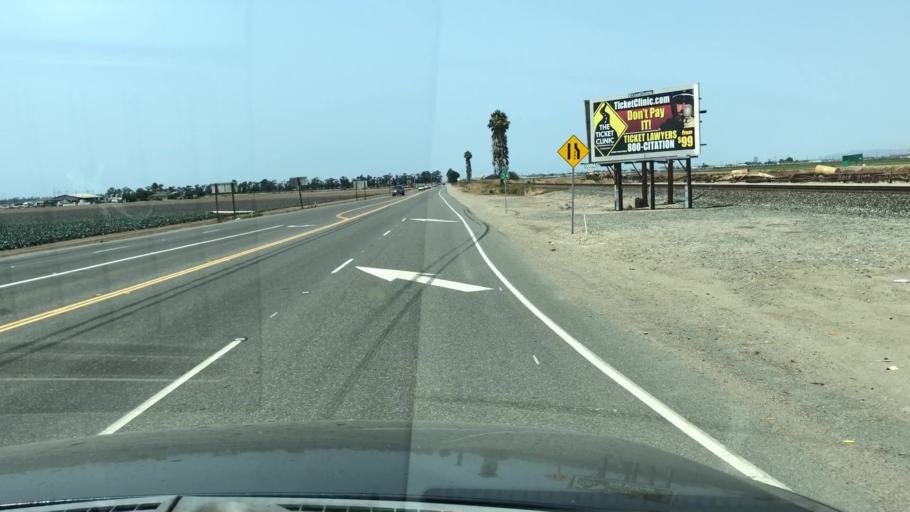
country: US
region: California
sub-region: Ventura County
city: Camarillo
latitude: 34.1964
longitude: -119.0701
